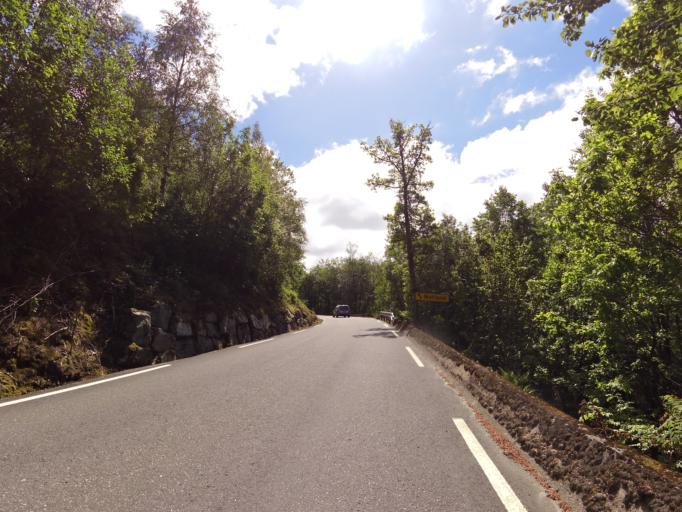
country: NO
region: Vest-Agder
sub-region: Kvinesdal
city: Liknes
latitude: 58.2894
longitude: 6.9388
